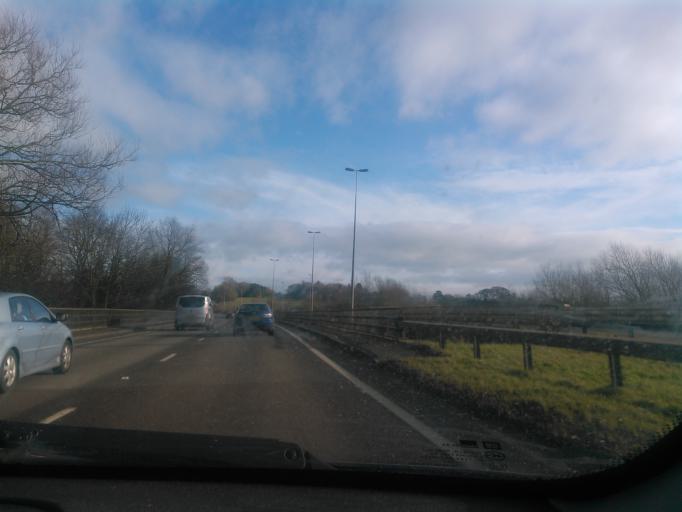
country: GB
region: England
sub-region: Staffordshire
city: Uttoxeter
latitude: 52.9071
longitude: -1.8456
